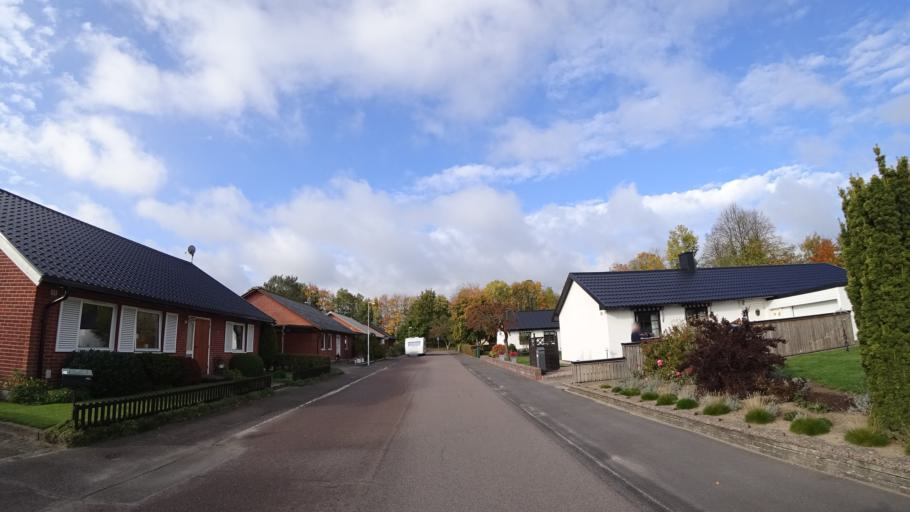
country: SE
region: Skane
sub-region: Staffanstorps Kommun
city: Staffanstorp
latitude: 55.6437
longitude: 13.1973
